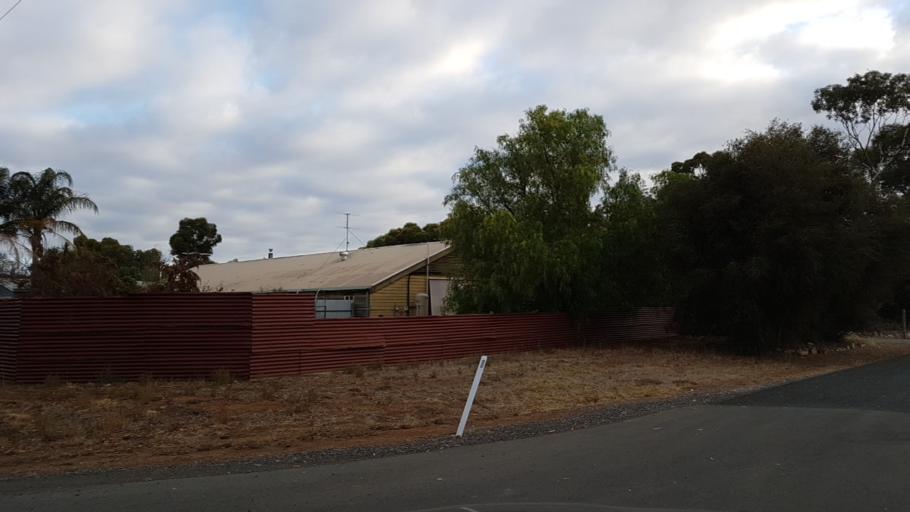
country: AU
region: South Australia
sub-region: Mount Barker
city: Callington
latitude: -35.1176
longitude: 139.0353
